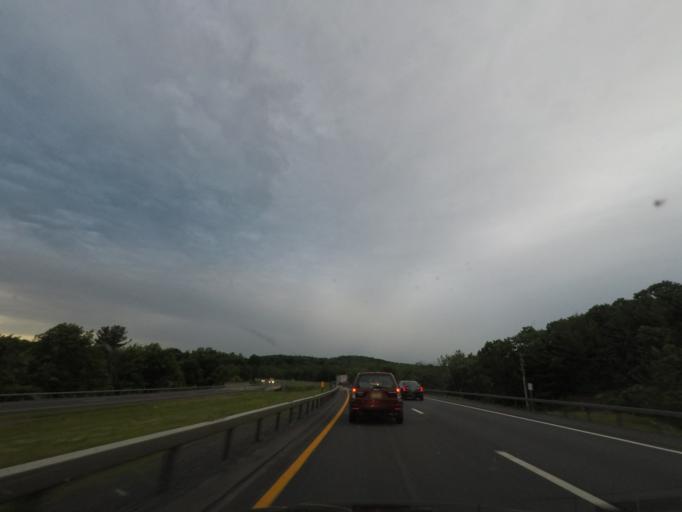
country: US
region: New York
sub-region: Columbia County
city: Chatham
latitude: 42.4397
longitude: -73.5552
